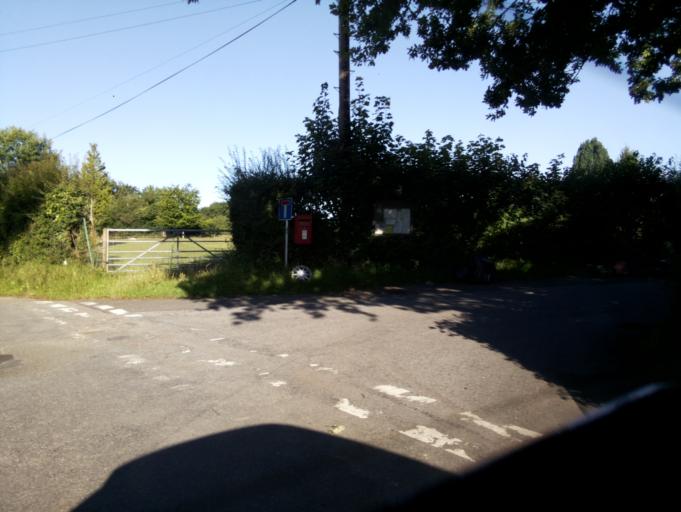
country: GB
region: Wales
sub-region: Monmouthshire
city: Llangwm
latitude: 51.6809
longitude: -2.7630
